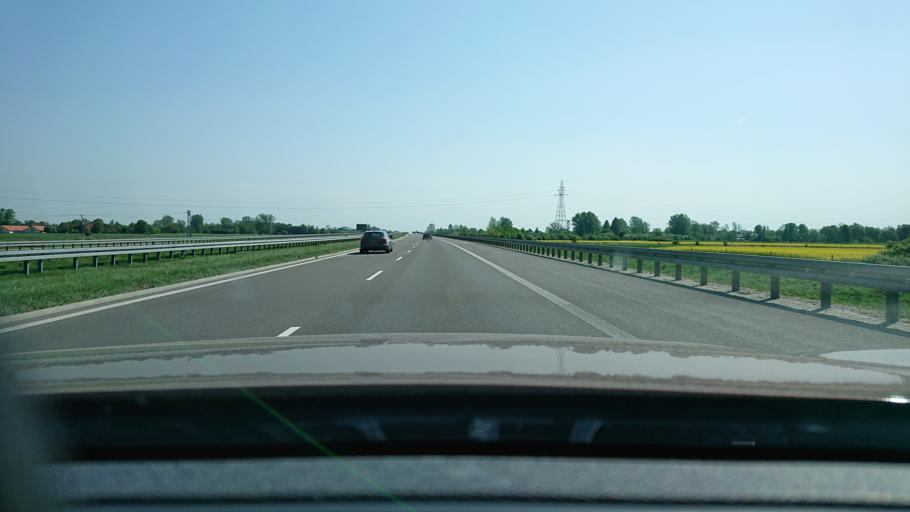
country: PL
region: Subcarpathian Voivodeship
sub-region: Powiat lancucki
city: Gluchow
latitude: 50.0985
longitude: 22.2433
